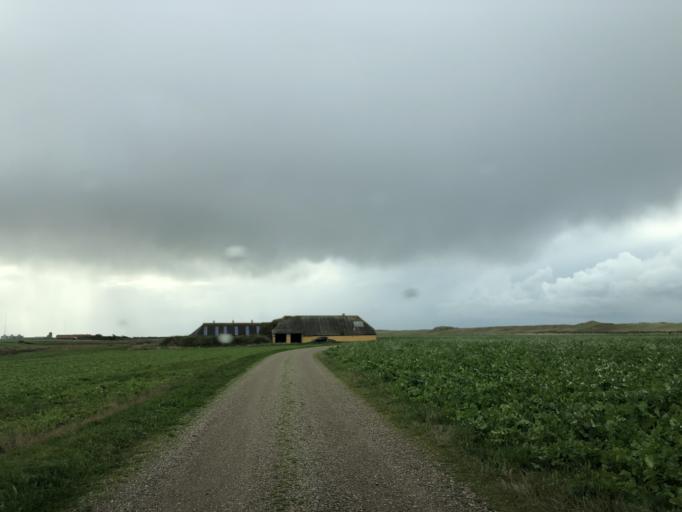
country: DK
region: Central Jutland
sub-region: Lemvig Kommune
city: Harboore
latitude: 56.4699
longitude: 8.1303
